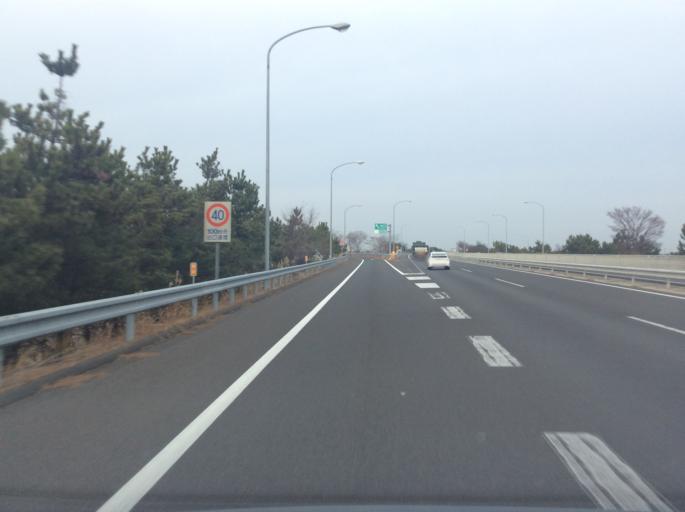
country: JP
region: Miyagi
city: Iwanuma
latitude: 38.1320
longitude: 140.8875
